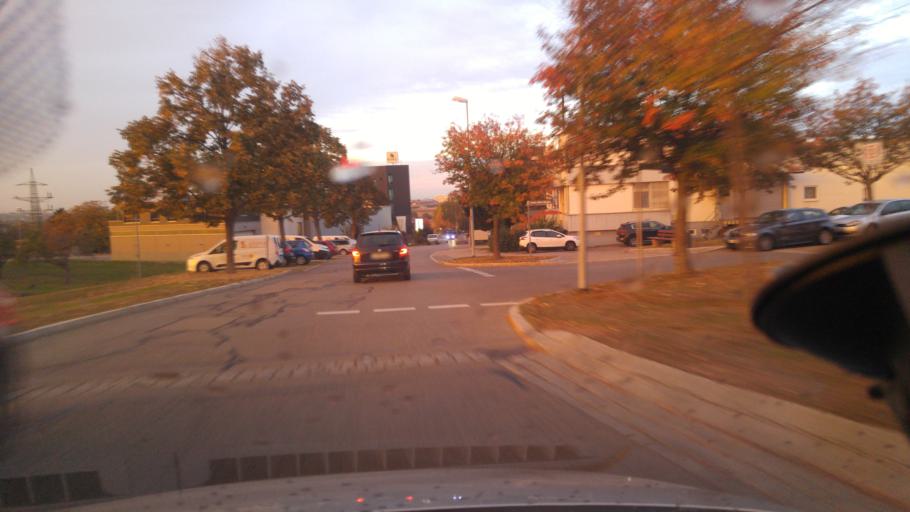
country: DE
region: Baden-Wuerttemberg
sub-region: Regierungsbezirk Stuttgart
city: Gerlingen
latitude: 48.7995
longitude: 9.0533
